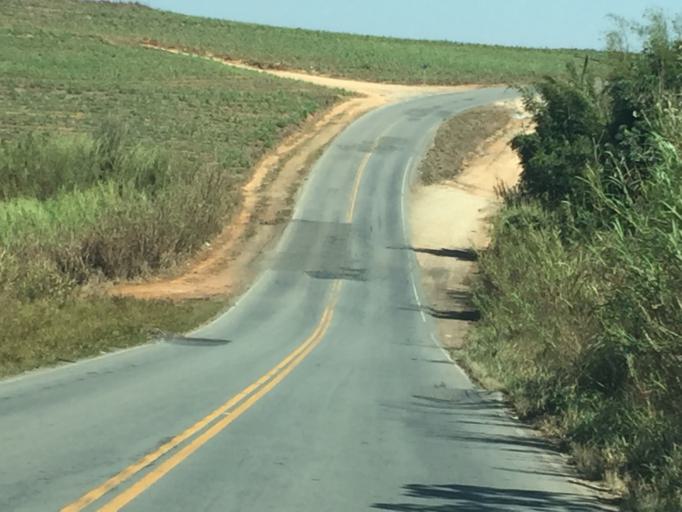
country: BR
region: Sao Paulo
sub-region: Itapira
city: Itapira
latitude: -22.3982
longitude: -46.8541
